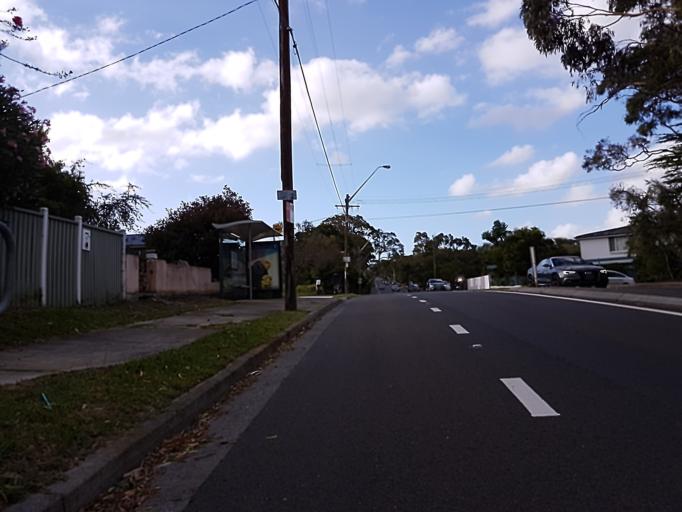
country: AU
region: New South Wales
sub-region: Manly Vale
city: Balgowlah
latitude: -33.7874
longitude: 151.2402
